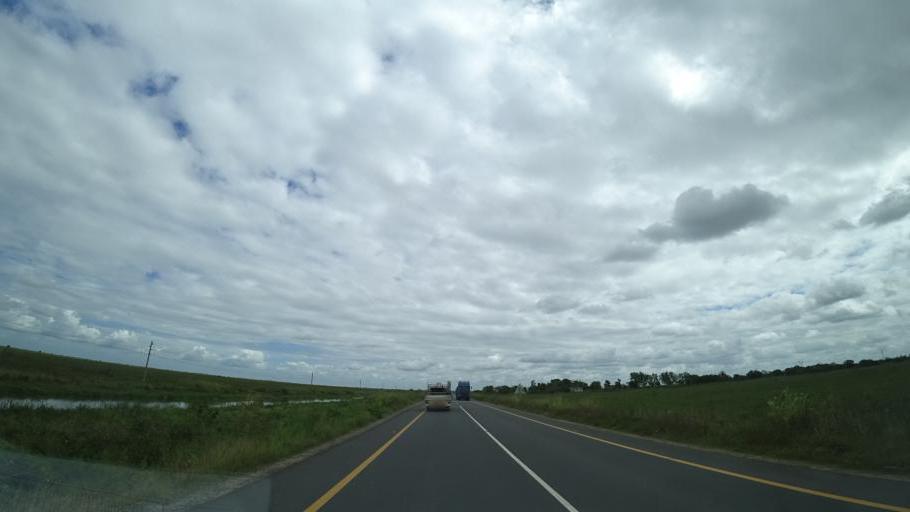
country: MZ
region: Sofala
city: Dondo
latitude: -19.4943
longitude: 34.5904
